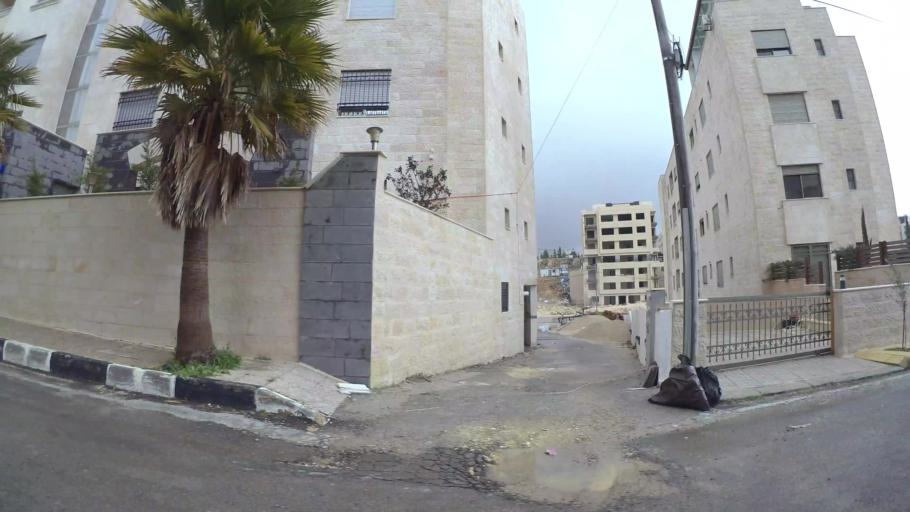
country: JO
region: Amman
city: Wadi as Sir
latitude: 31.9396
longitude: 35.8514
